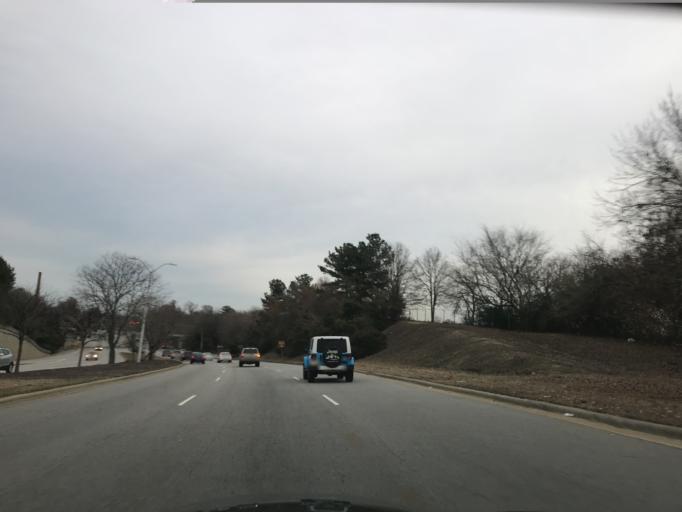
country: US
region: North Carolina
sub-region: Wake County
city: Raleigh
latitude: 35.7690
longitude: -78.6434
